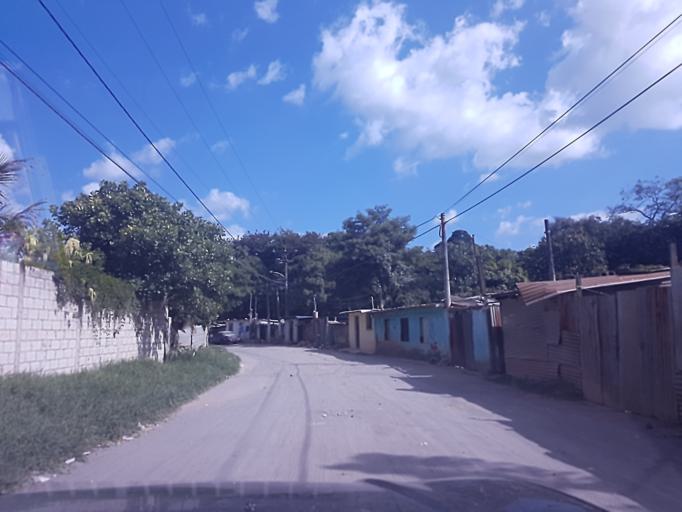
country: GT
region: Guatemala
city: Petapa
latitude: 14.5046
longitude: -90.5591
